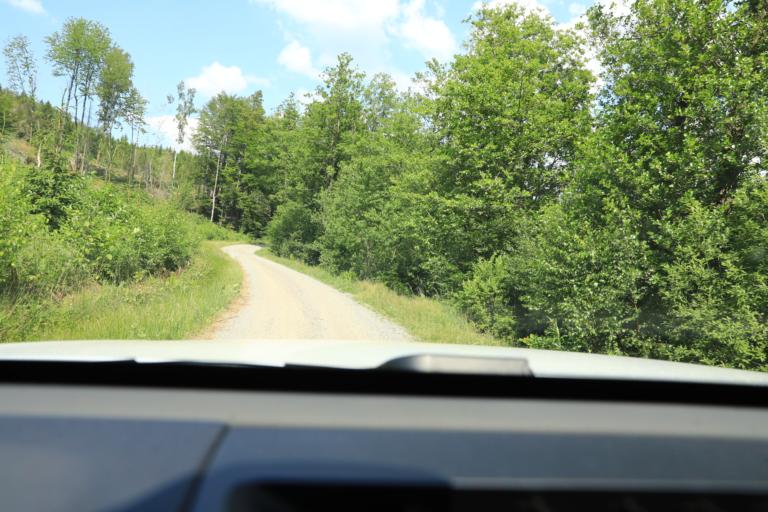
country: SE
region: Halland
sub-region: Varbergs Kommun
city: Veddige
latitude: 57.2107
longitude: 12.3492
